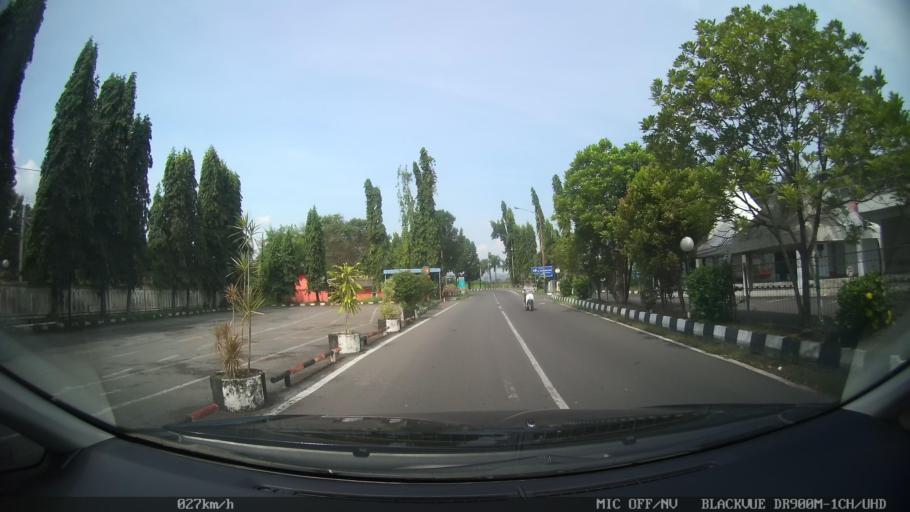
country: ID
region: Daerah Istimewa Yogyakarta
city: Depok
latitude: -7.7852
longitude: 110.4388
